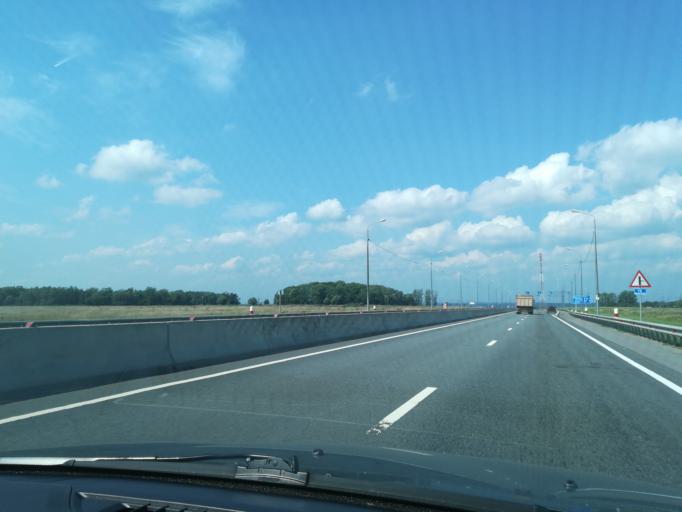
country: RU
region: Leningrad
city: Kingisepp
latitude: 59.5904
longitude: 28.7532
